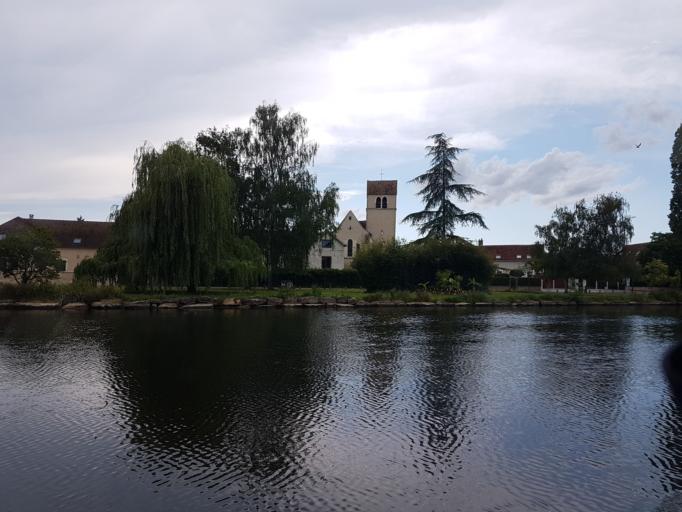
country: FR
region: Bourgogne
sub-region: Departement de l'Yonne
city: Moneteau
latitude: 47.8487
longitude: 3.5780
